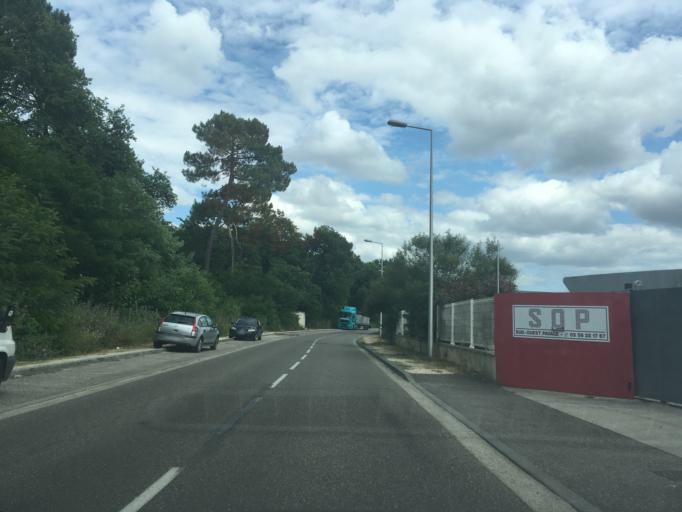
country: FR
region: Aquitaine
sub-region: Departement de la Gironde
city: Eysines
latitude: 44.8711
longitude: -0.6604
